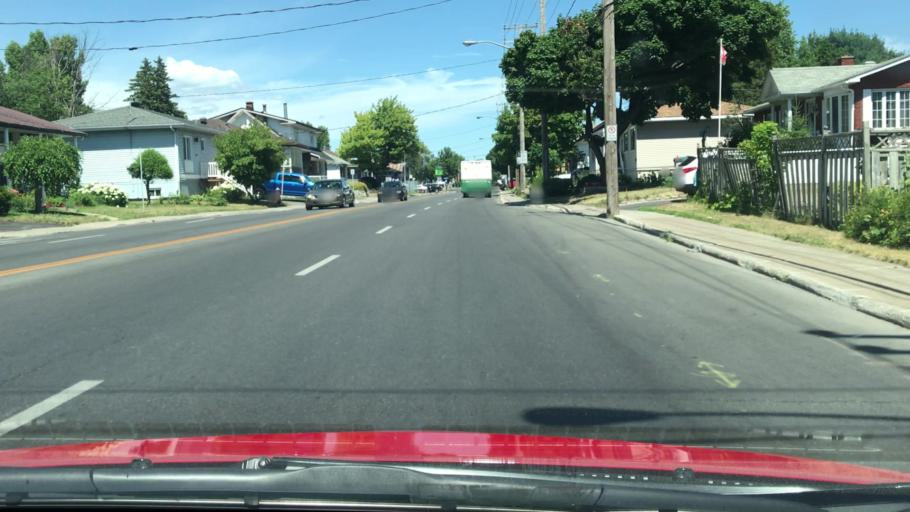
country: CA
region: Quebec
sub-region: Laval
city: Laval
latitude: 45.5358
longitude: -73.7463
